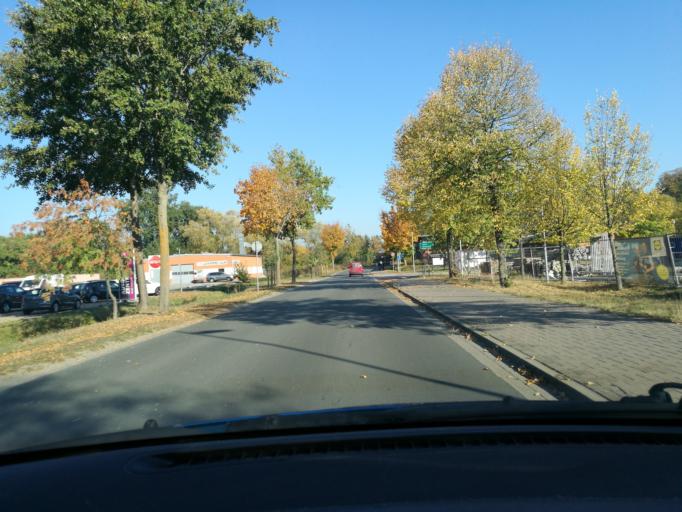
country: DE
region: Lower Saxony
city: Dannenberg
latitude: 53.1030
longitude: 11.1018
